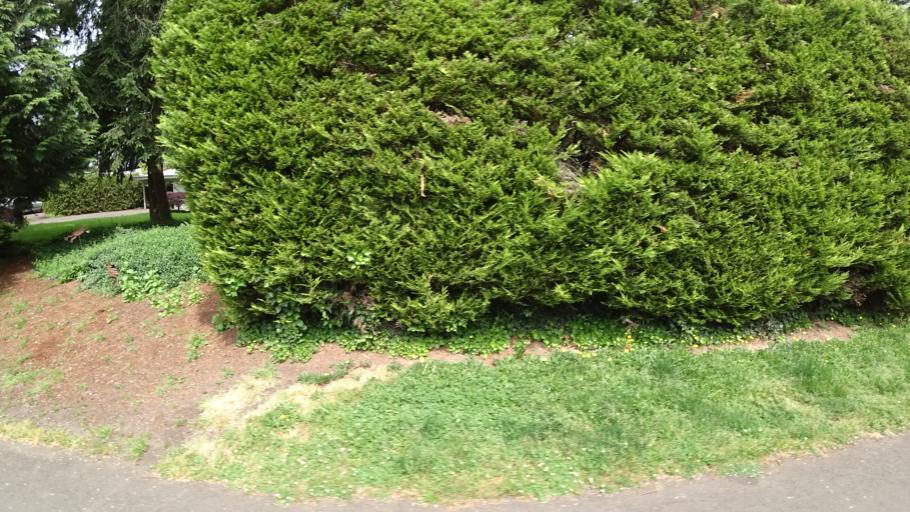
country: US
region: Oregon
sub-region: Washington County
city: Garden Home-Whitford
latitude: 45.4723
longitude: -122.7364
